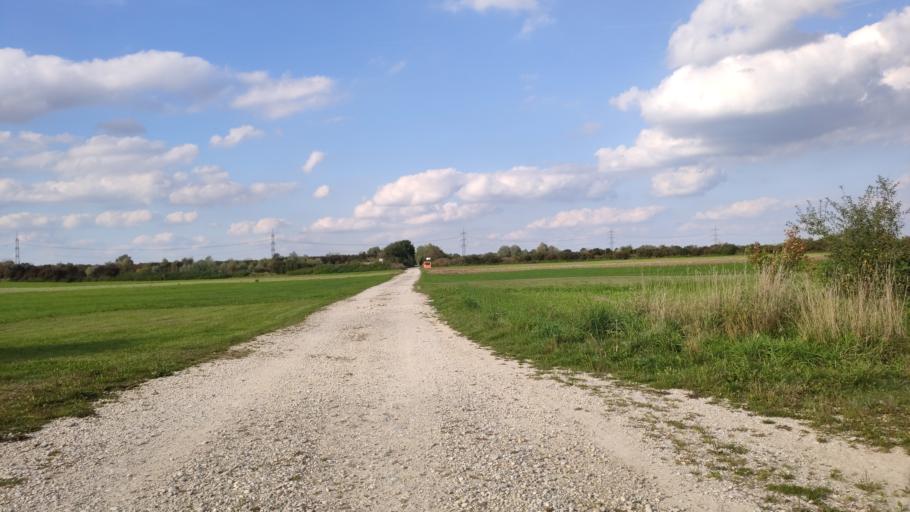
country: DE
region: Bavaria
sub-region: Swabia
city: Oberottmarshausen
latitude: 48.2229
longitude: 10.8743
